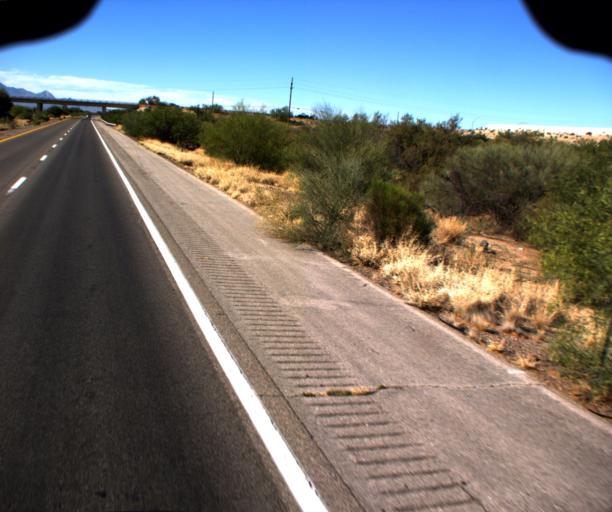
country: US
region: Arizona
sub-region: Pima County
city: Sahuarita
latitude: 31.9602
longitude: -110.9882
